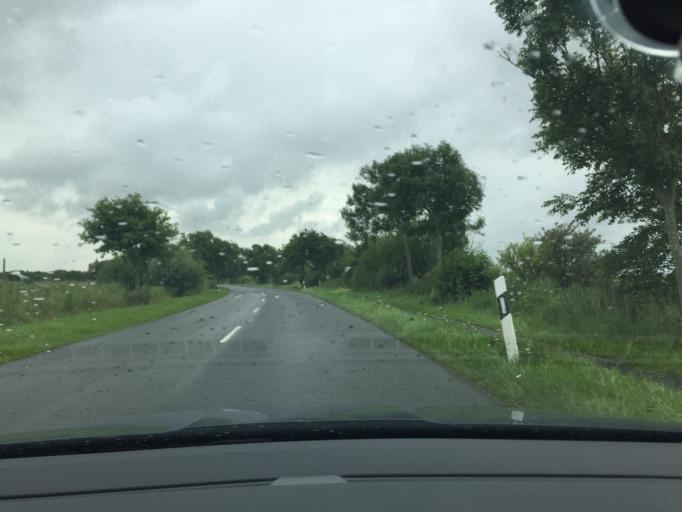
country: DE
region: Lower Saxony
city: Wirdum
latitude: 53.4924
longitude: 7.0652
